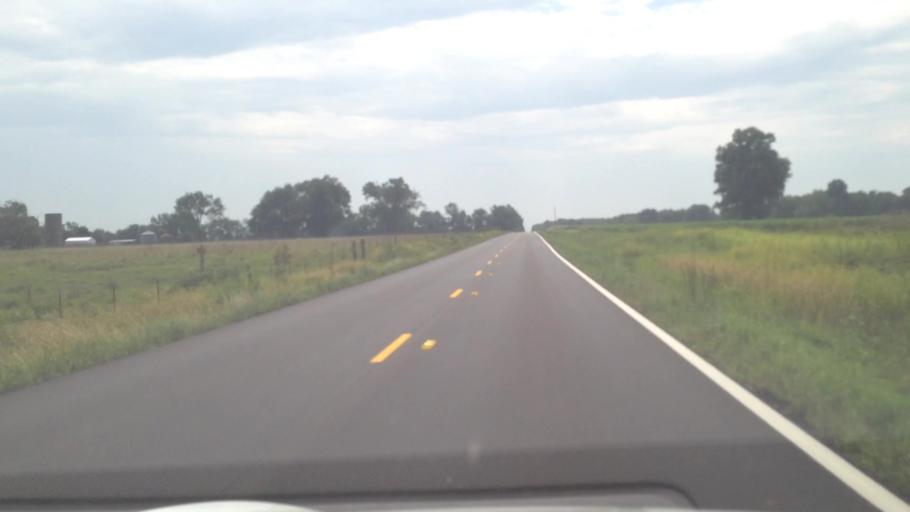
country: US
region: Kansas
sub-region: Crawford County
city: Girard
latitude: 37.5322
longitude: -94.9606
